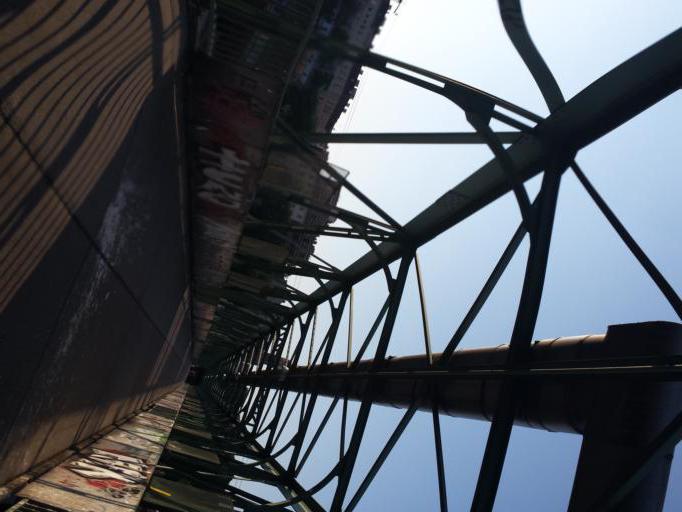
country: AT
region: Vienna
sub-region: Wien Stadt
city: Vienna
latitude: 48.1933
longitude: 16.3264
